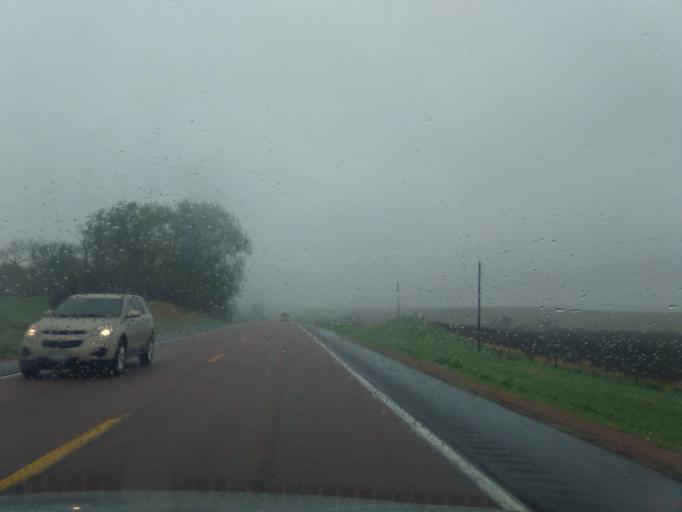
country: US
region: Nebraska
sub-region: Wayne County
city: Wayne
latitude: 42.2357
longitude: -97.1056
